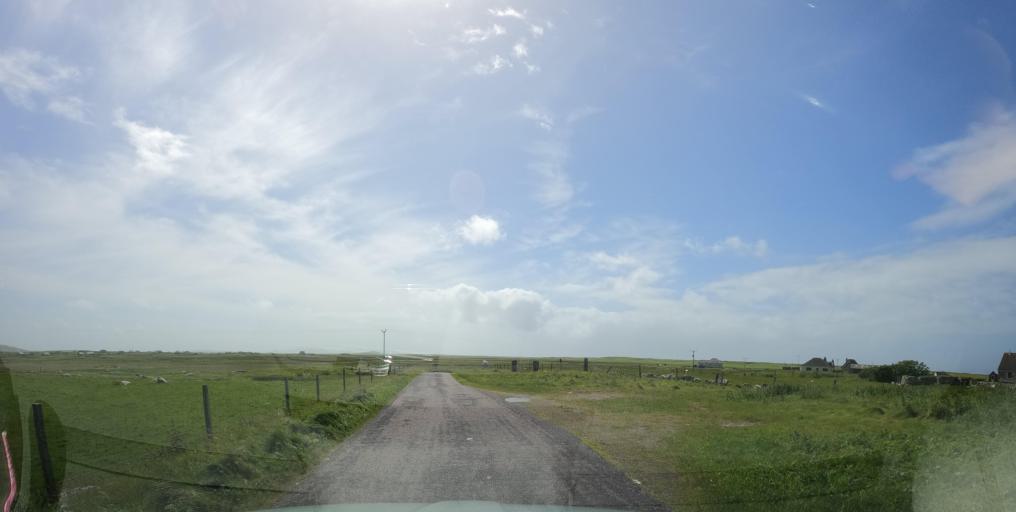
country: GB
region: Scotland
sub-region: Eilean Siar
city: Isle of South Uist
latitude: 57.1646
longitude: -7.3880
